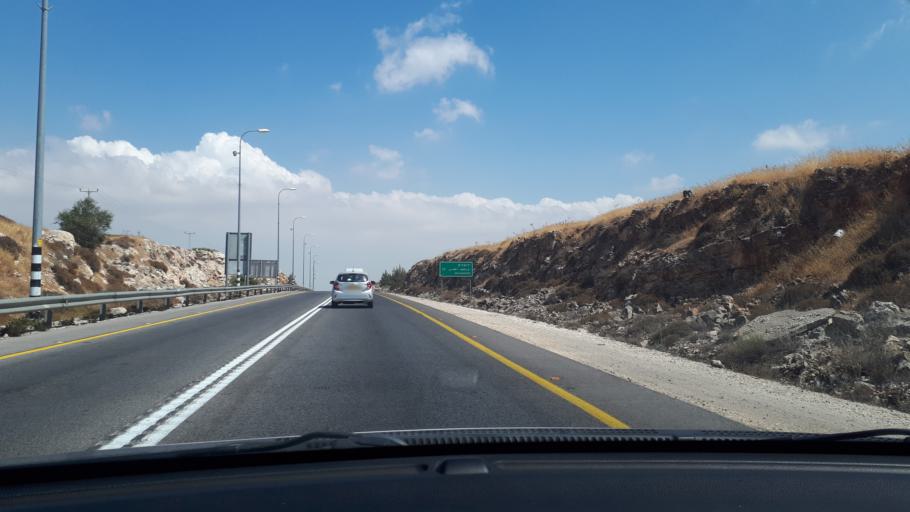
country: PS
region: West Bank
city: Burqah
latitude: 31.9092
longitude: 35.2522
